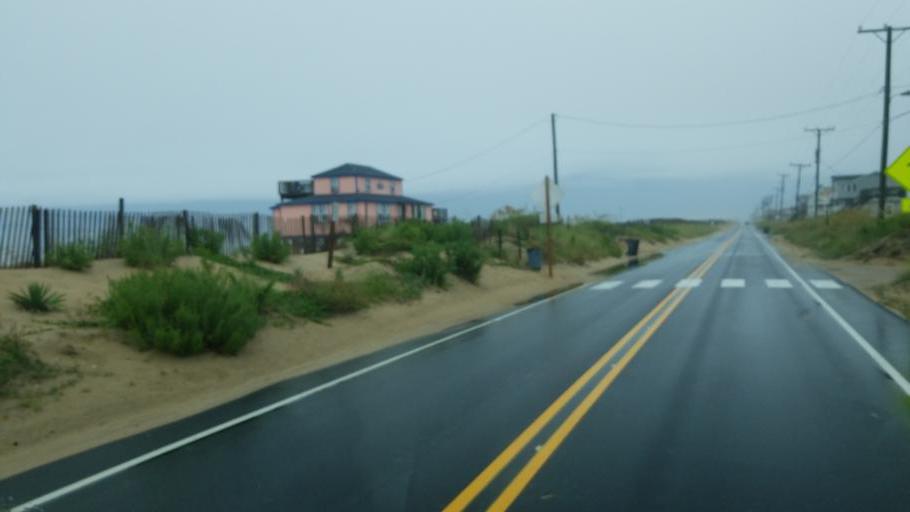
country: US
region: North Carolina
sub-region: Dare County
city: Kitty Hawk
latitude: 36.0702
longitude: -75.6927
